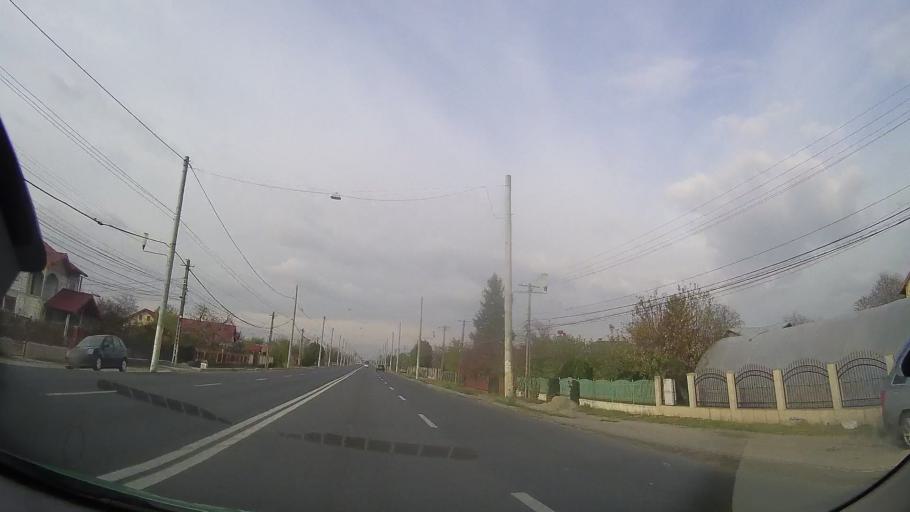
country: RO
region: Prahova
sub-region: Comuna Barcanesti
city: Tatarani
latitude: 44.8930
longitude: 26.0438
